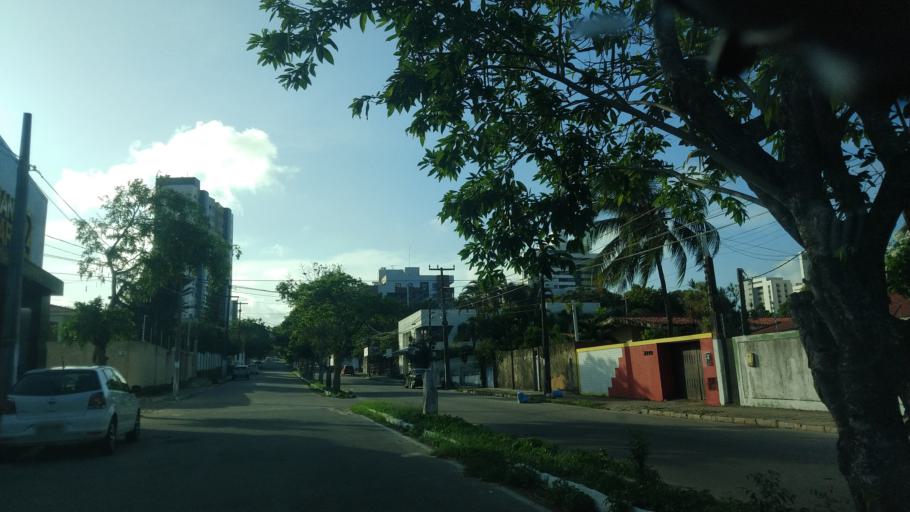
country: BR
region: Rio Grande do Norte
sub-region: Natal
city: Natal
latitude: -5.8202
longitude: -35.2023
